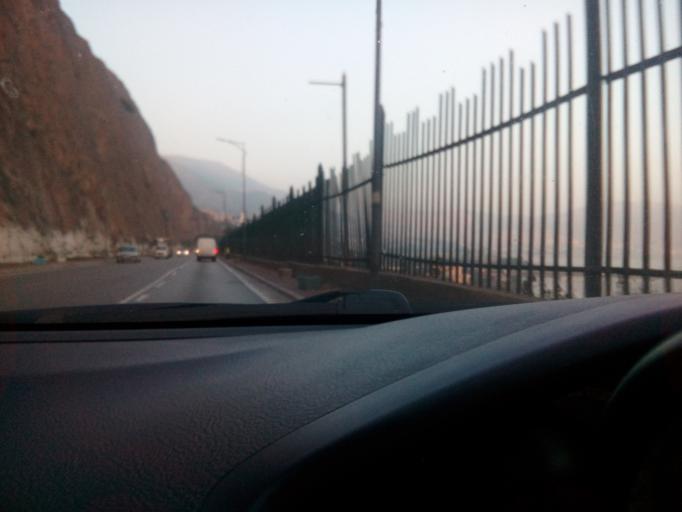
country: DZ
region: Oran
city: Mers el Kebir
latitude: 35.7119
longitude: -0.6785
